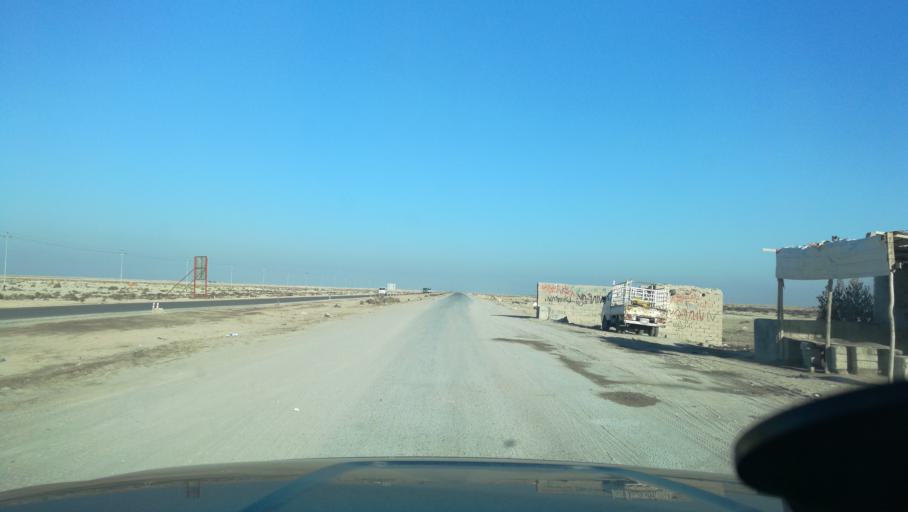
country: IQ
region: Dhi Qar
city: Suq ash Shuyukh
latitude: 30.8325
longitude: 46.3609
